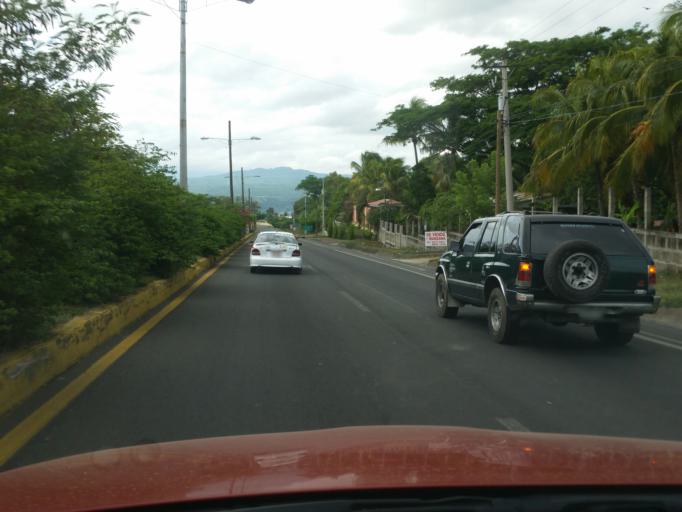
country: NI
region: Masaya
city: Nindiri
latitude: 12.0044
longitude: -86.1347
